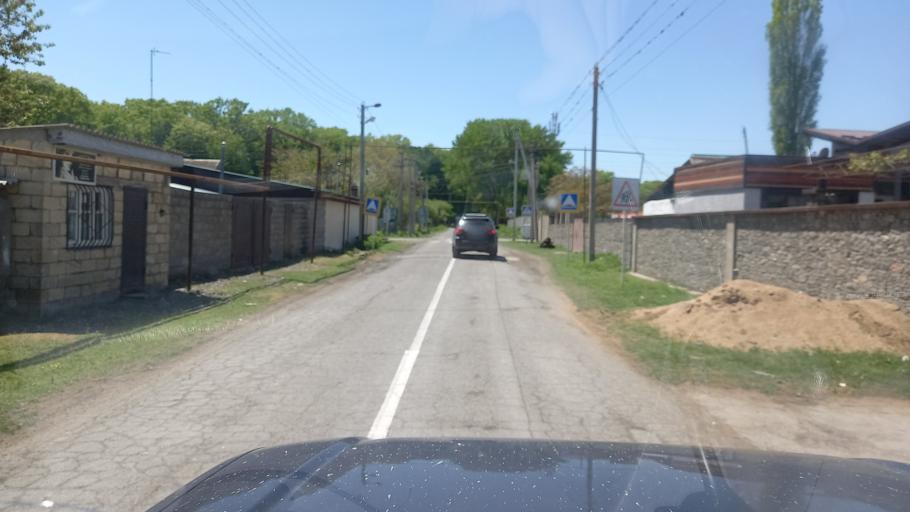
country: RU
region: Dagestan
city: Samur
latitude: 41.8449
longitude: 48.5824
